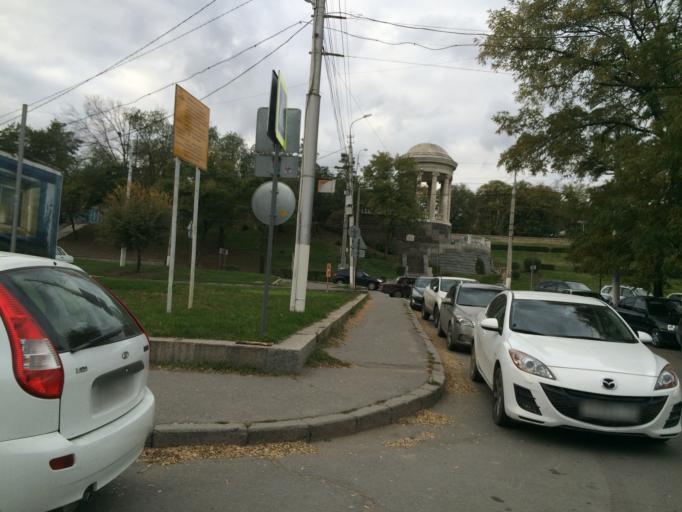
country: RU
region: Volgograd
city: Volgograd
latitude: 48.7017
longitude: 44.5196
